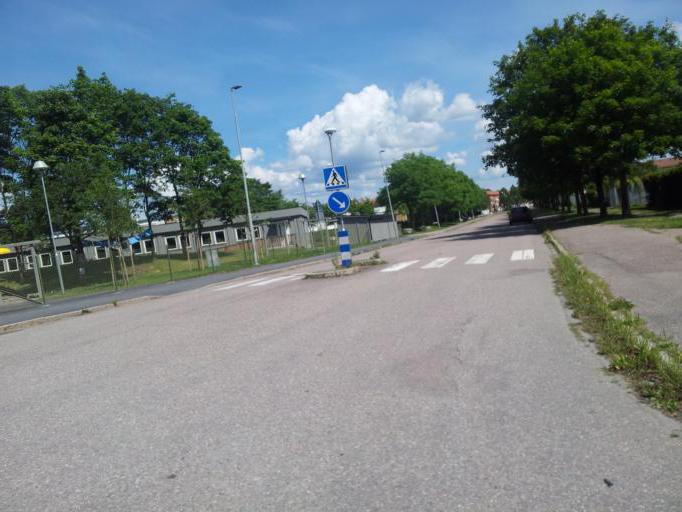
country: SE
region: Uppsala
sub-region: Uppsala Kommun
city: Uppsala
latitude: 59.8627
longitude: 17.6649
